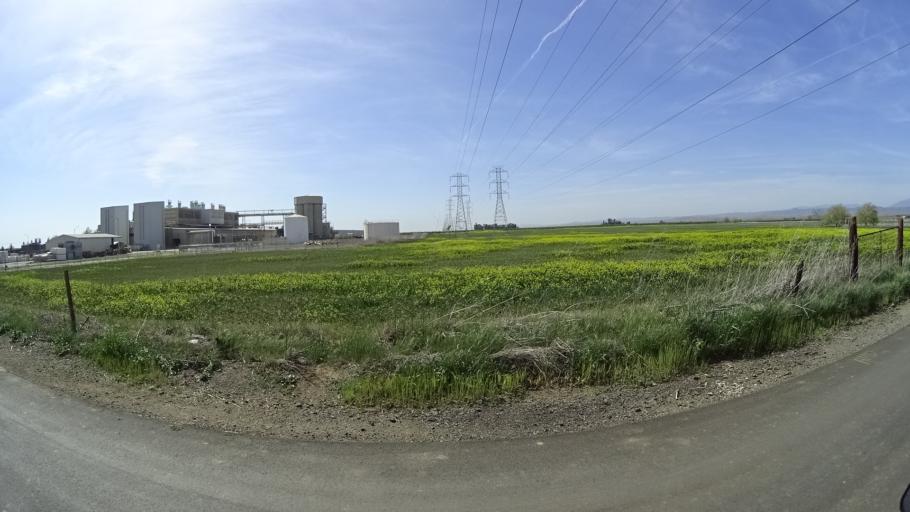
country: US
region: California
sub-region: Glenn County
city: Willows
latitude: 39.5390
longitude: -122.2638
